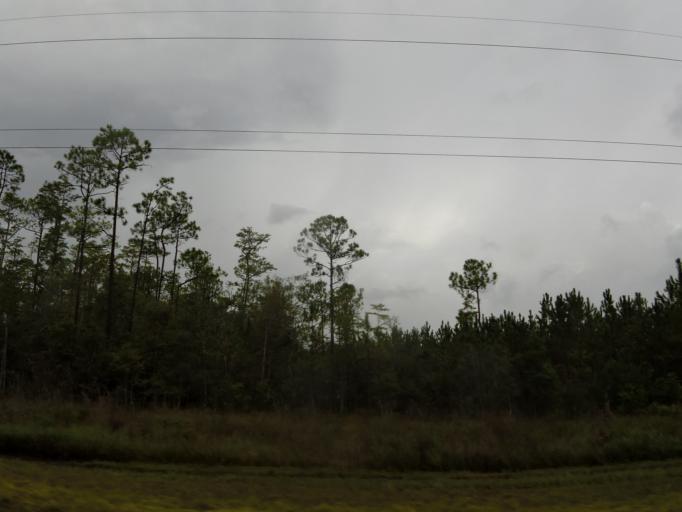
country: US
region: Florida
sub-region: Duval County
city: Baldwin
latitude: 30.4761
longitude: -82.0500
